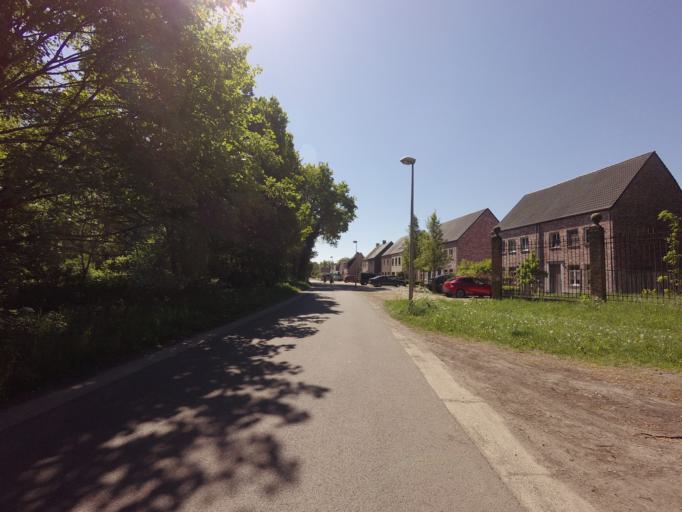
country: BE
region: Flanders
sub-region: Provincie Antwerpen
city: Essen
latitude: 51.4628
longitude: 4.4484
